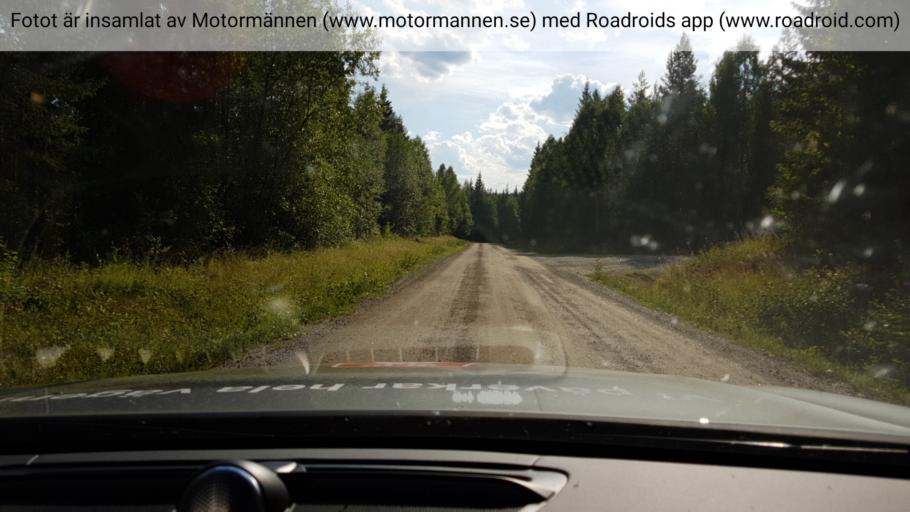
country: SE
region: Vaesternorrland
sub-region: Solleftea Kommun
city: As
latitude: 63.7818
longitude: 16.3620
